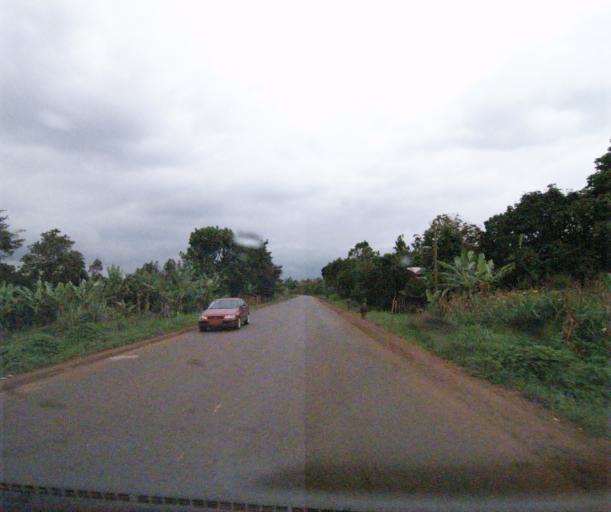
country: CM
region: West
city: Bansoa
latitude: 5.4848
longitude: 10.2129
